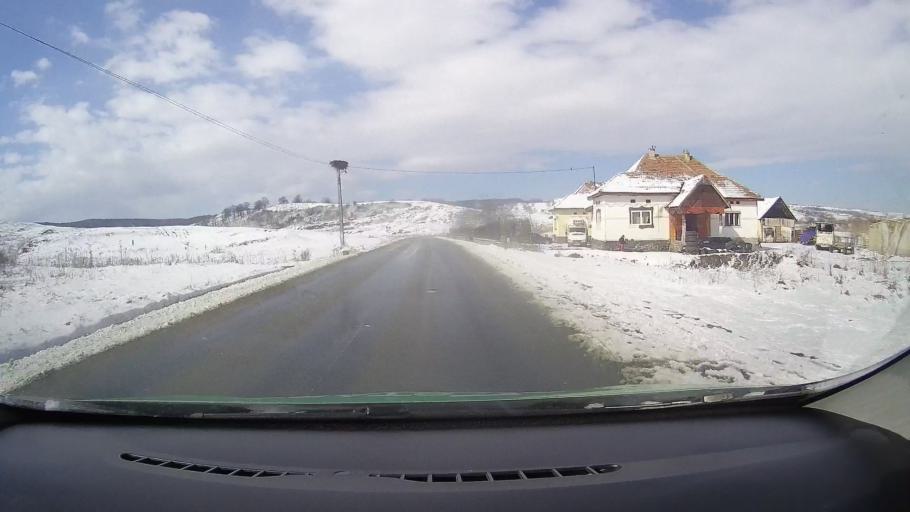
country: RO
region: Sibiu
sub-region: Comuna Altina
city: Altina
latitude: 45.9397
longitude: 24.4555
